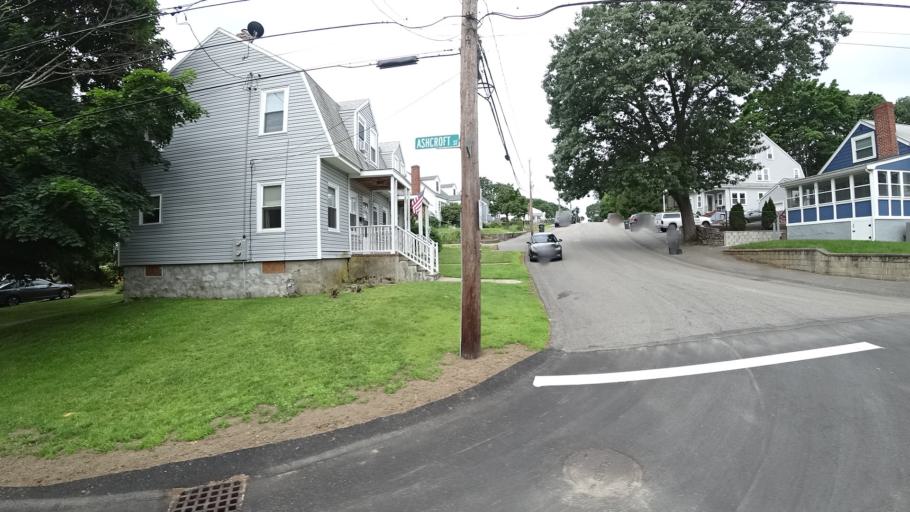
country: US
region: Massachusetts
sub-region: Norfolk County
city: Dedham
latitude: 42.2365
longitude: -71.1458
